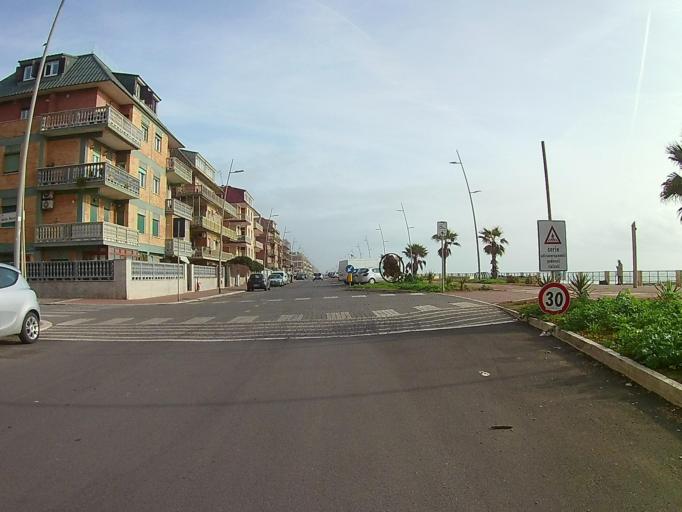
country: IT
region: Latium
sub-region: Citta metropolitana di Roma Capitale
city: Lido di Ostia
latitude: 41.7370
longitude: 12.2543
